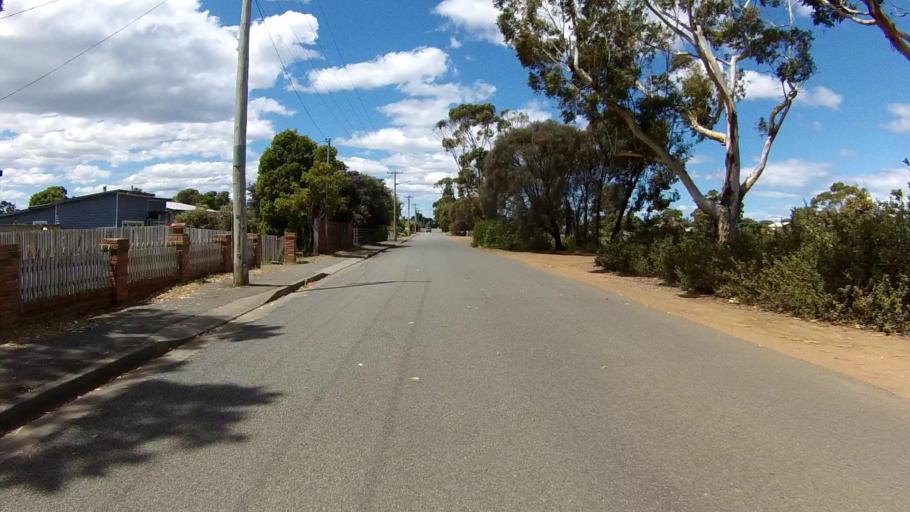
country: AU
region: Tasmania
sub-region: Clarence
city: Lauderdale
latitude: -42.9118
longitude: 147.4897
